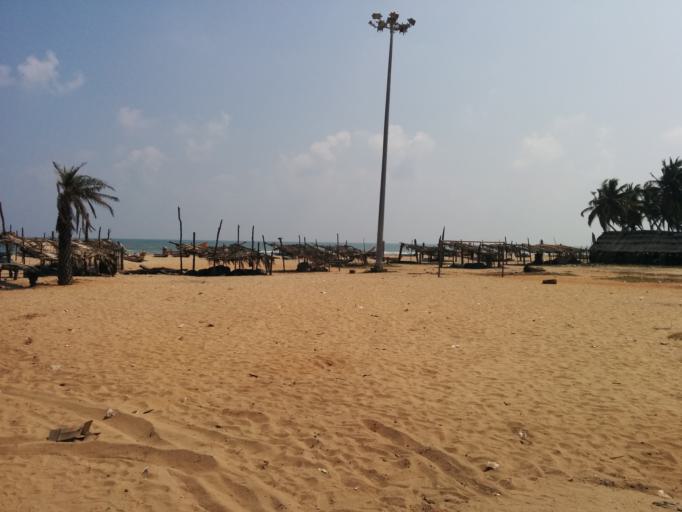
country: IN
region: Pondicherry
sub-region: Puducherry
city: Puducherry
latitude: 11.8662
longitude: 79.8177
